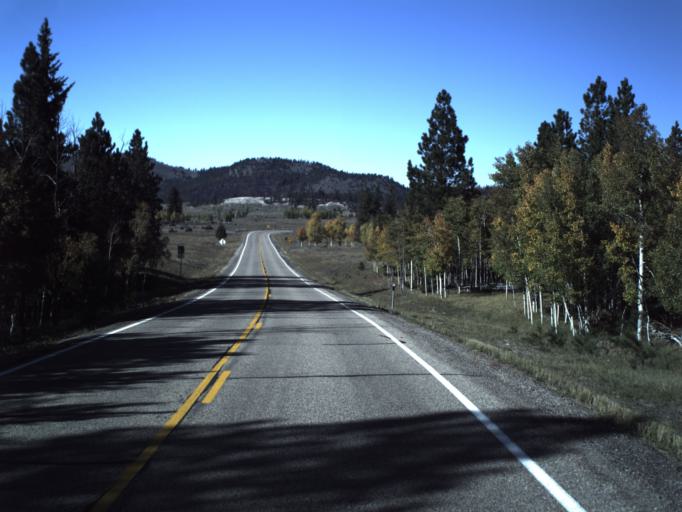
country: US
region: Utah
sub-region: Iron County
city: Parowan
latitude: 37.6730
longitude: -112.6671
